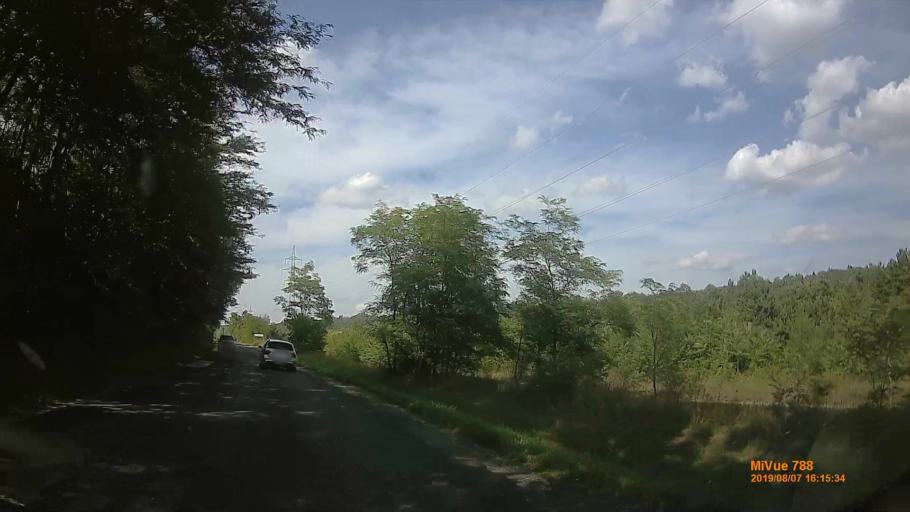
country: HU
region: Zala
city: Gyenesdias
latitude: 46.8021
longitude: 17.2703
